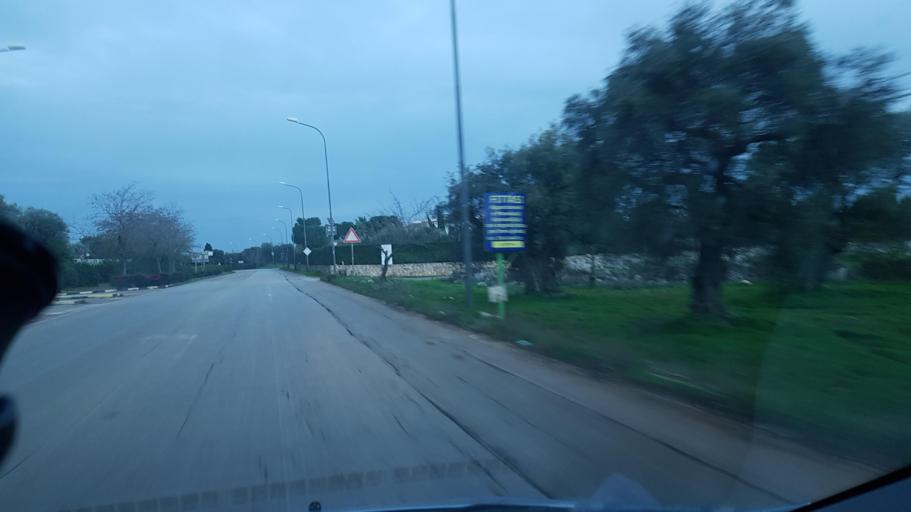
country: IT
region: Apulia
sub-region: Provincia di Brindisi
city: Ceglie Messapica
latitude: 40.6440
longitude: 17.5348
